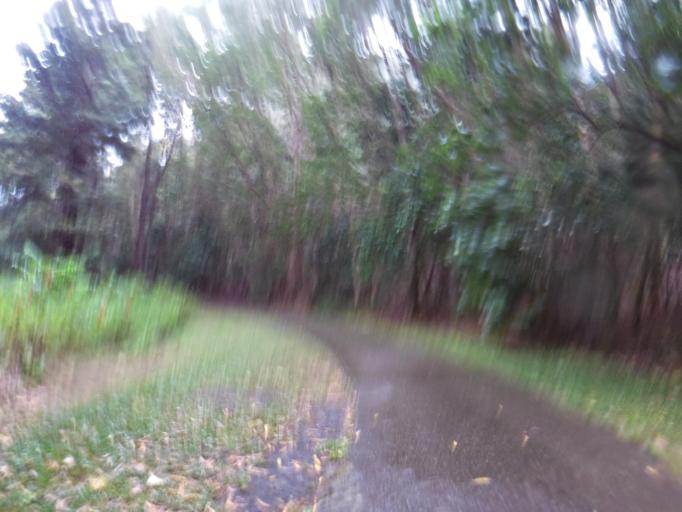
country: AU
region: Queensland
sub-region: Cairns
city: Cairns
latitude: -16.8926
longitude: 145.7510
